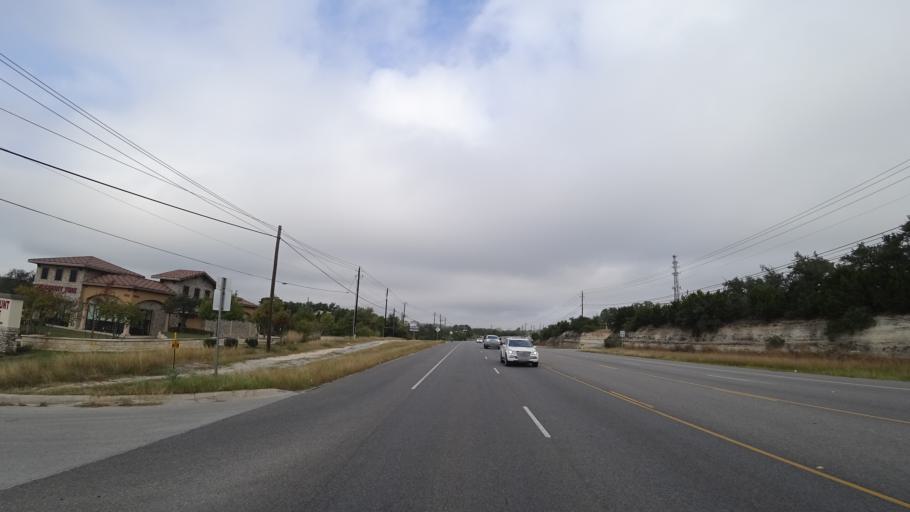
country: US
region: Texas
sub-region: Travis County
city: Bee Cave
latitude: 30.3129
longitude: -97.9475
